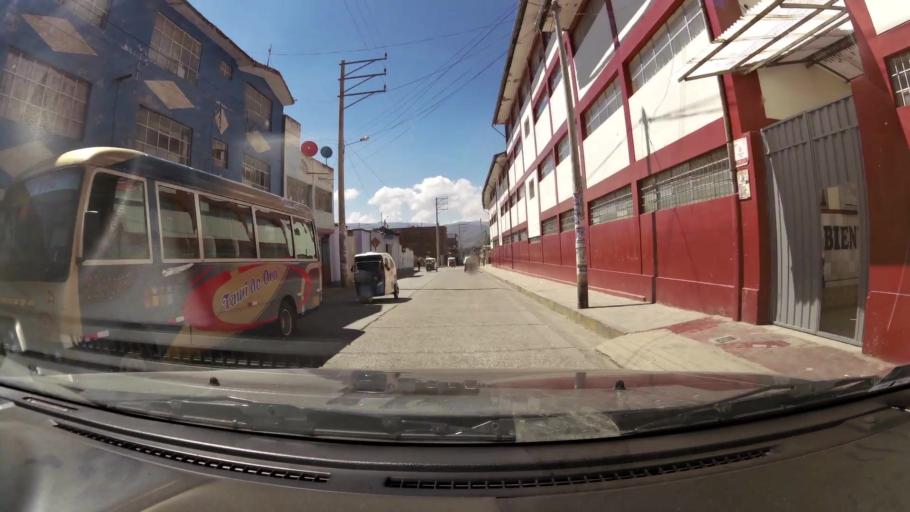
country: PE
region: Junin
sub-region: Provincia de Jauja
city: Jauja
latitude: -11.7756
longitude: -75.4963
